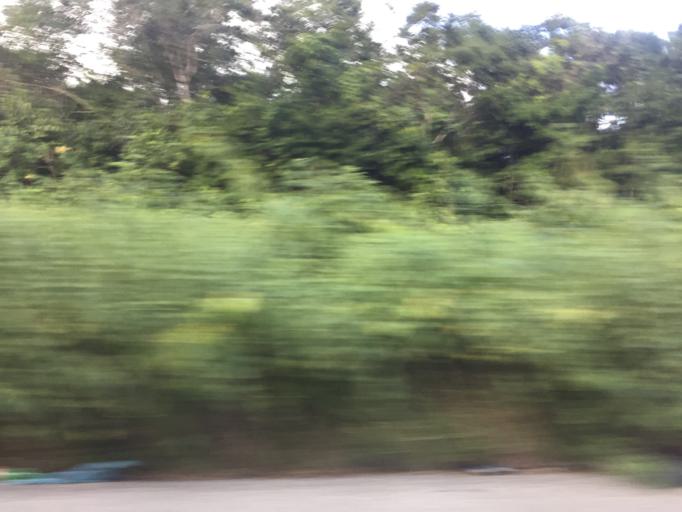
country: MX
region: Quintana Roo
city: Tulum
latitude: 20.2822
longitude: -87.4946
